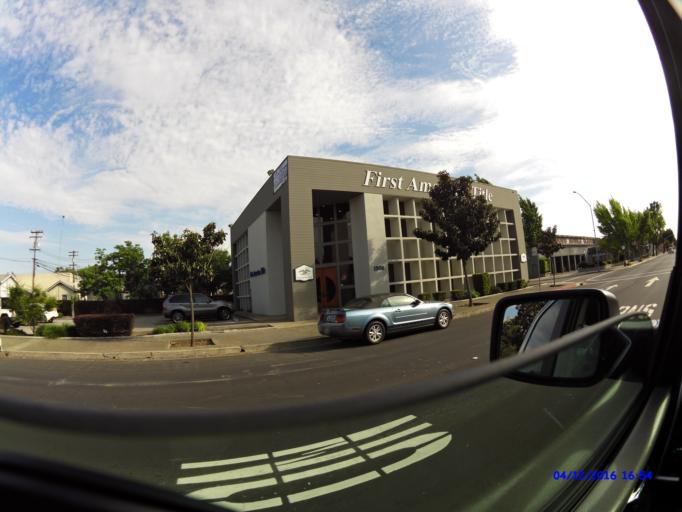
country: US
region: California
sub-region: Stanislaus County
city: Modesto
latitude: 37.6424
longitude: -120.9929
